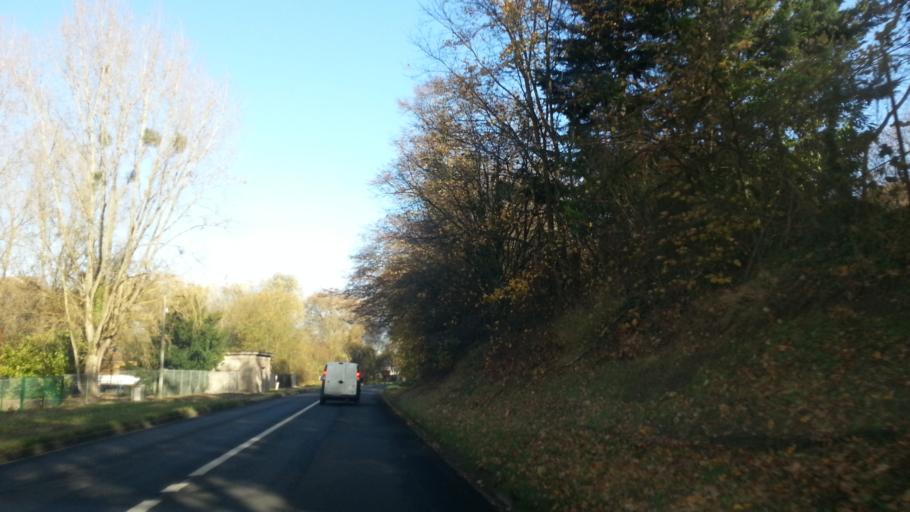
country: FR
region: Picardie
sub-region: Departement de l'Oise
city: Villers-Saint-Paul
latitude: 49.2747
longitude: 2.4987
